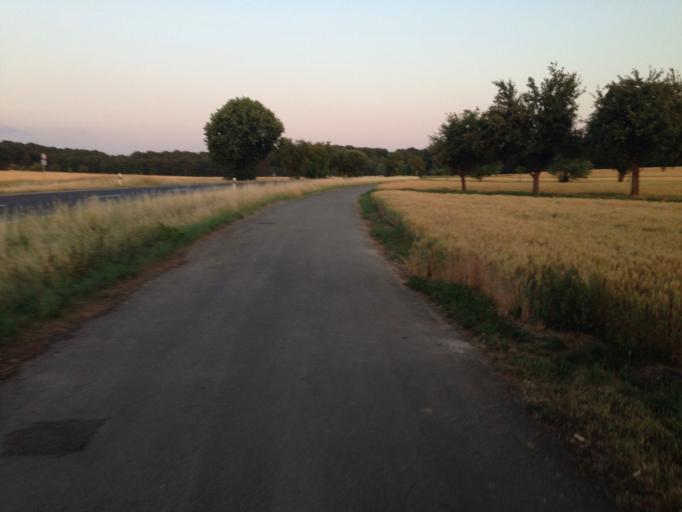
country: DE
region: Hesse
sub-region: Regierungsbezirk Giessen
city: Grossen Buseck
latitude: 50.5736
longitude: 8.7626
